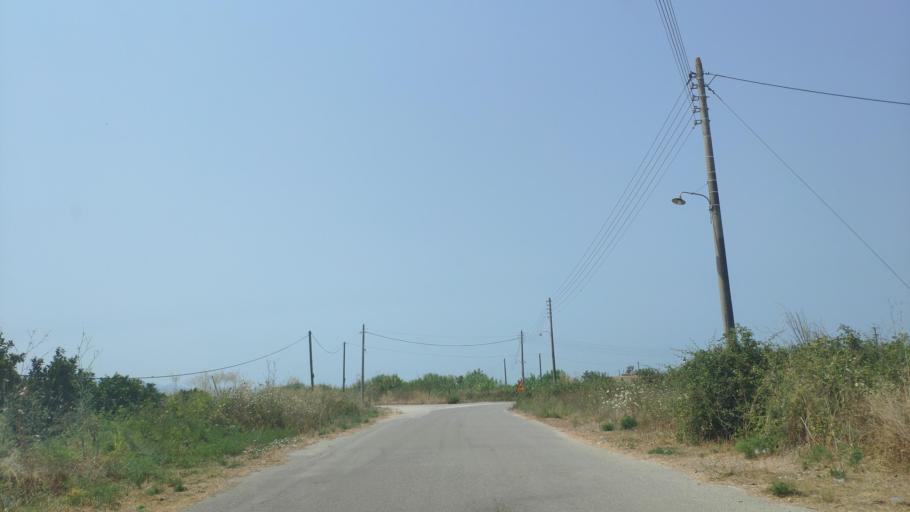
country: GR
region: Epirus
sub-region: Nomos Artas
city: Neochori
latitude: 39.0613
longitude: 21.0504
